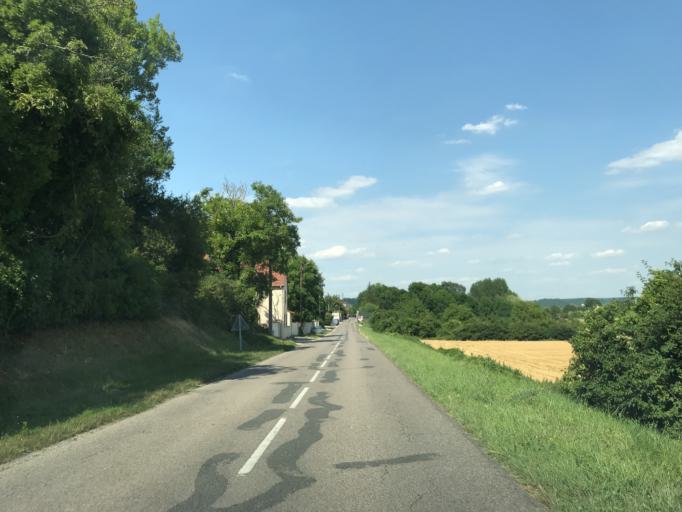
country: FR
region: Ile-de-France
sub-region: Departement des Yvelines
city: Freneuse
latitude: 49.0576
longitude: 1.5967
